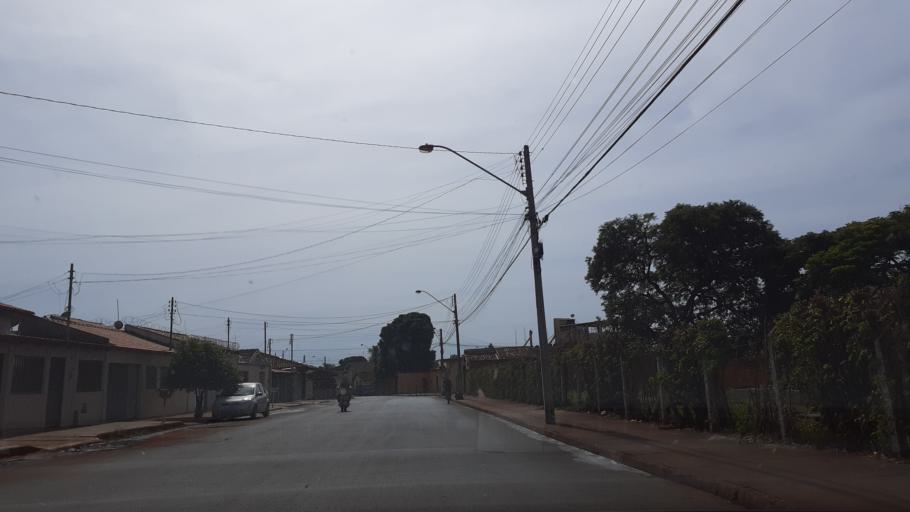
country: BR
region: Goias
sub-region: Itumbiara
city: Itumbiara
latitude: -18.4144
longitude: -49.2311
